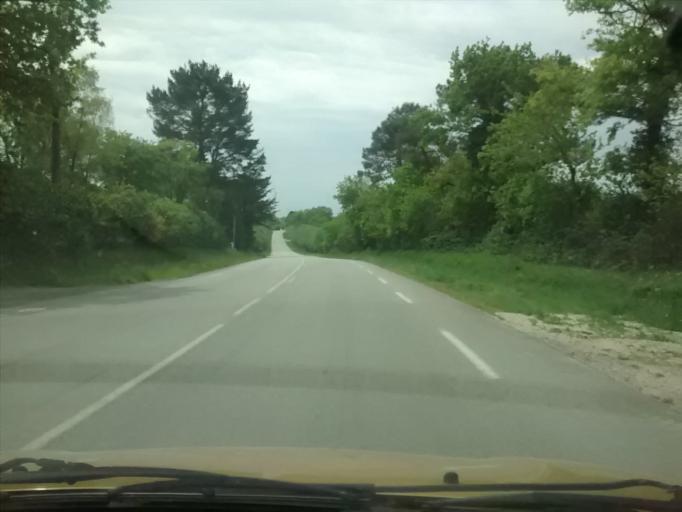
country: FR
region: Brittany
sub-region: Departement du Morbihan
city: Berric
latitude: 47.6241
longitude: -2.5344
